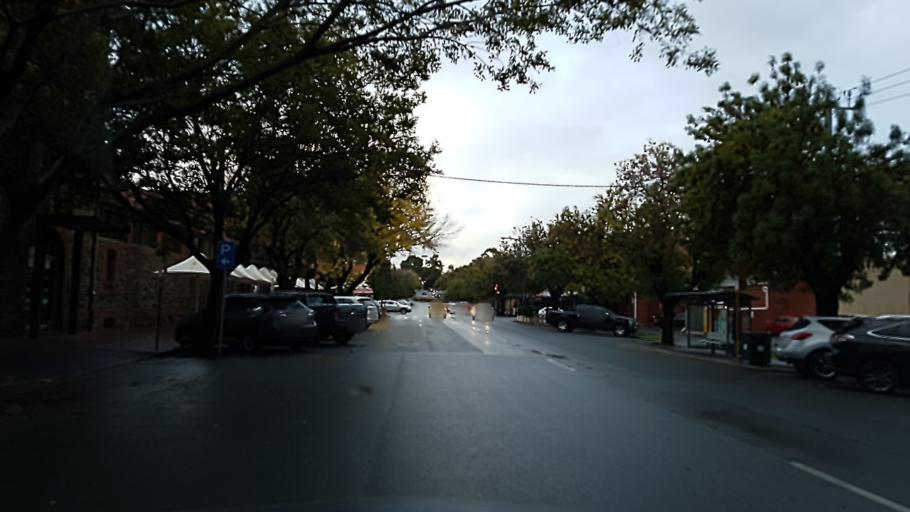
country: AU
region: South Australia
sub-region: Adelaide
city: North Adelaide
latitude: -34.9083
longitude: 138.6064
